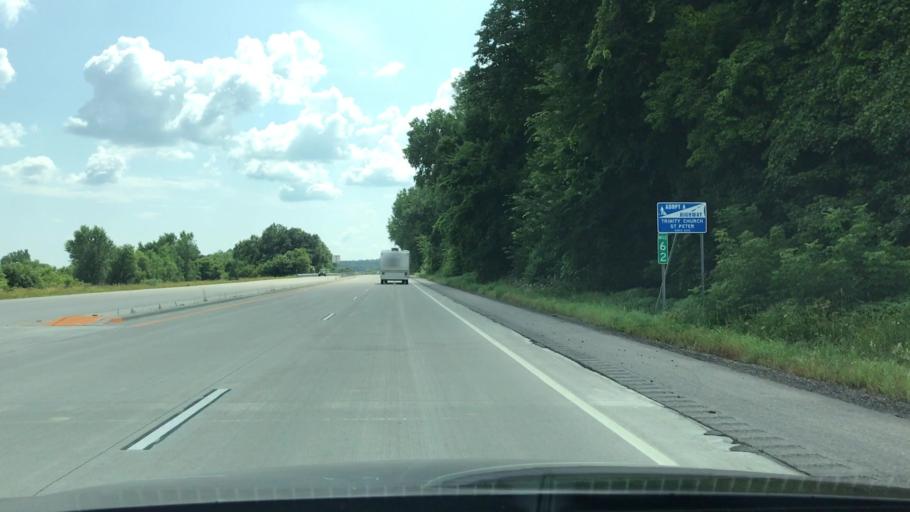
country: US
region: Minnesota
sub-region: Nicollet County
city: Saint Peter
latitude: 44.2787
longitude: -94.0120
